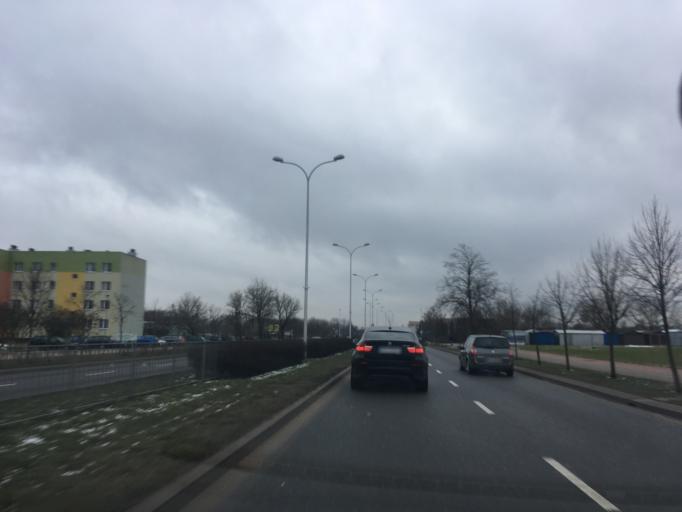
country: PL
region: Podlasie
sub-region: Suwalki
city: Suwalki
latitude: 54.1158
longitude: 22.9286
